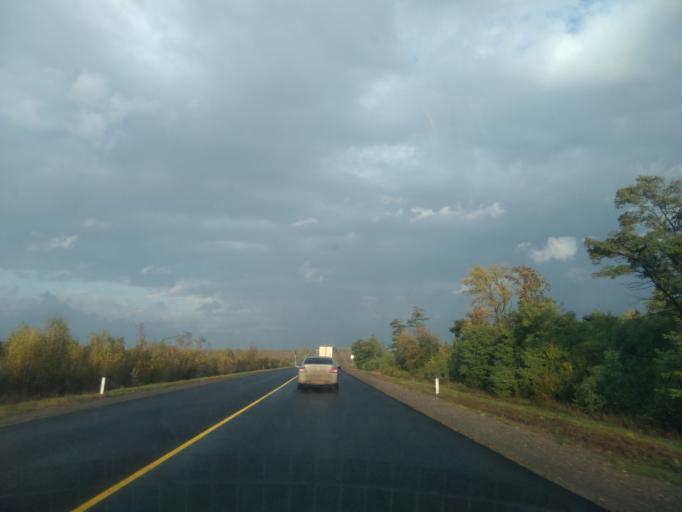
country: RU
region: Lipetsk
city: Donskoye
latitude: 52.5681
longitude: 38.7756
